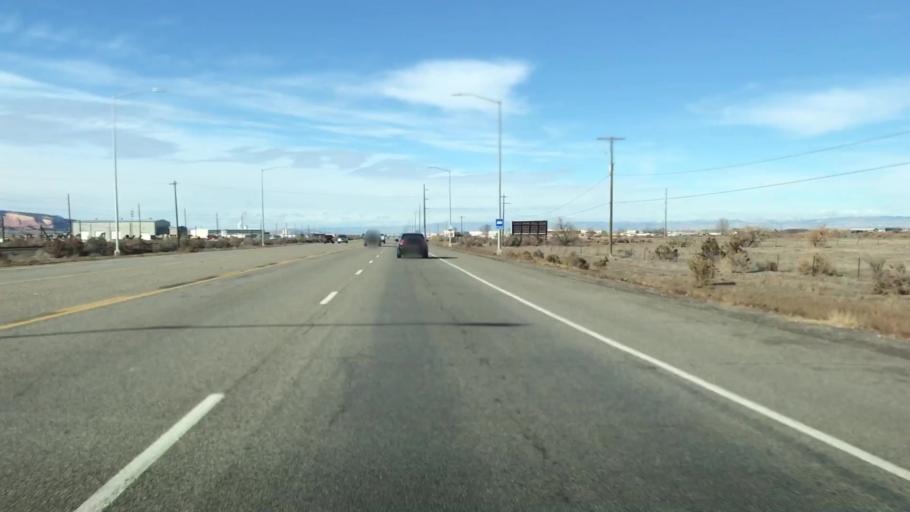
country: US
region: Colorado
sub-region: Mesa County
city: Redlands
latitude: 39.0951
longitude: -108.6157
